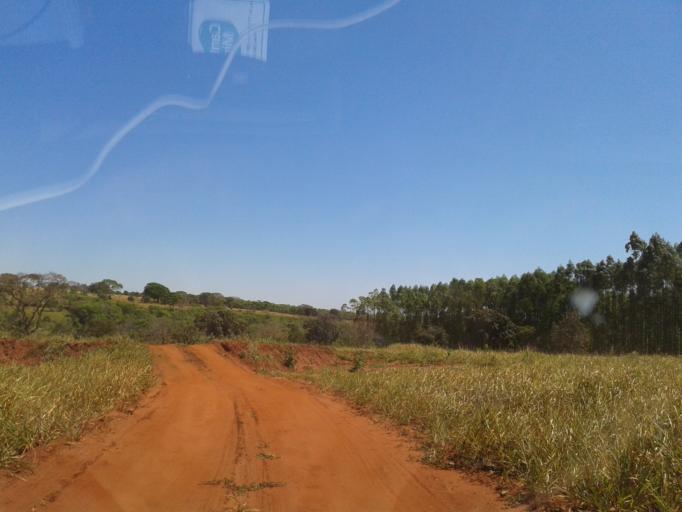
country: BR
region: Minas Gerais
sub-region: Ituiutaba
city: Ituiutaba
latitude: -19.0907
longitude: -49.2574
